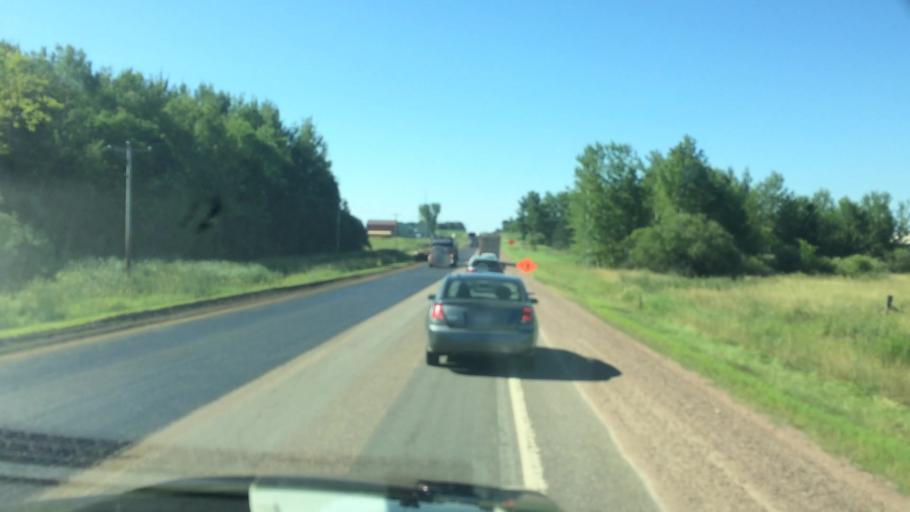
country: US
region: Wisconsin
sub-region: Marathon County
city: Stratford
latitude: 44.8962
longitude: -90.0788
